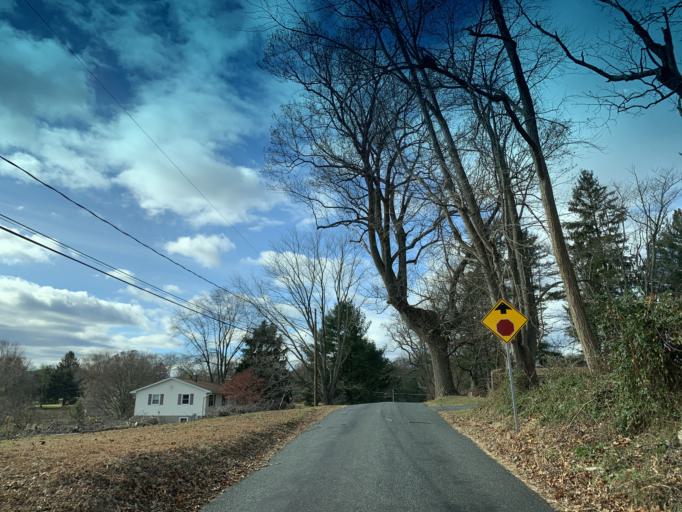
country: US
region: Maryland
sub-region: Harford County
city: Jarrettsville
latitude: 39.5949
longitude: -76.4192
